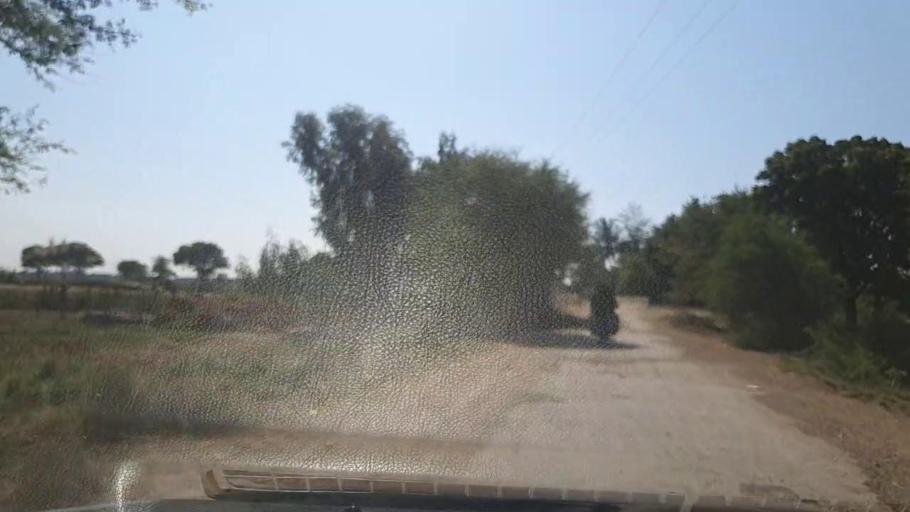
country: PK
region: Sindh
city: Mirpur Sakro
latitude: 24.5990
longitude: 67.7842
